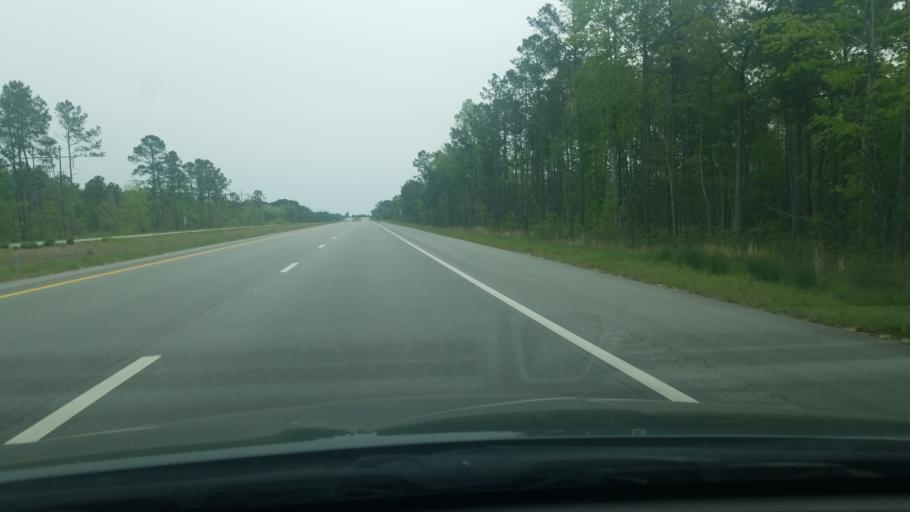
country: US
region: North Carolina
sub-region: Craven County
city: River Bend
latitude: 35.0427
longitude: -77.2197
